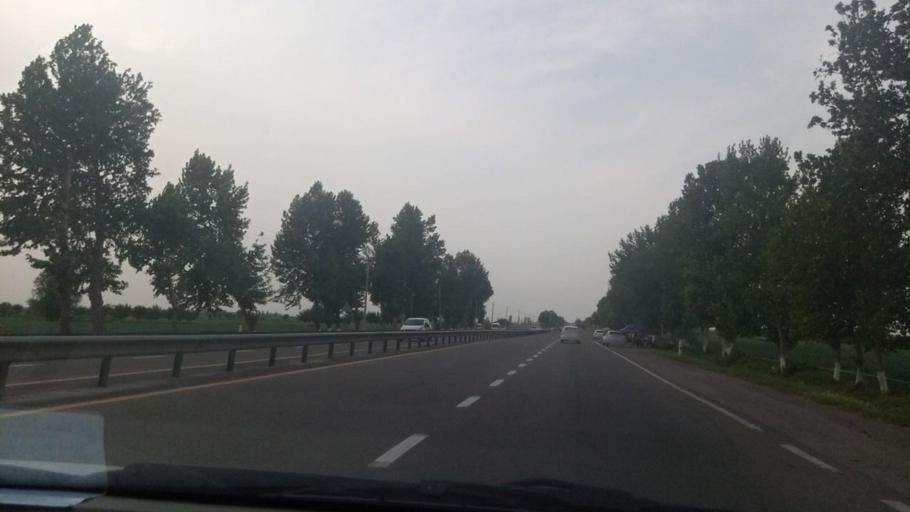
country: UZ
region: Toshkent Shahri
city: Bektemir
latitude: 41.1562
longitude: 69.4237
